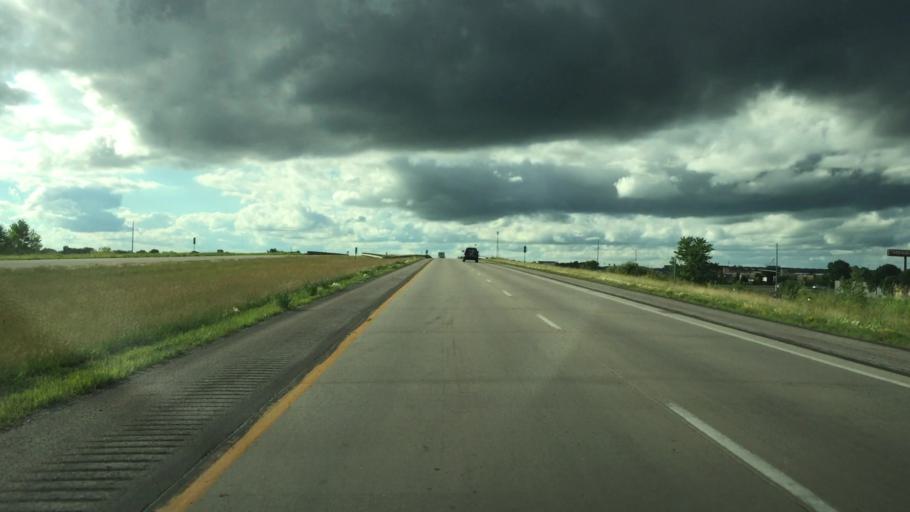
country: US
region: Iowa
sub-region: Polk County
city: Altoona
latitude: 41.6454
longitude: -93.5111
